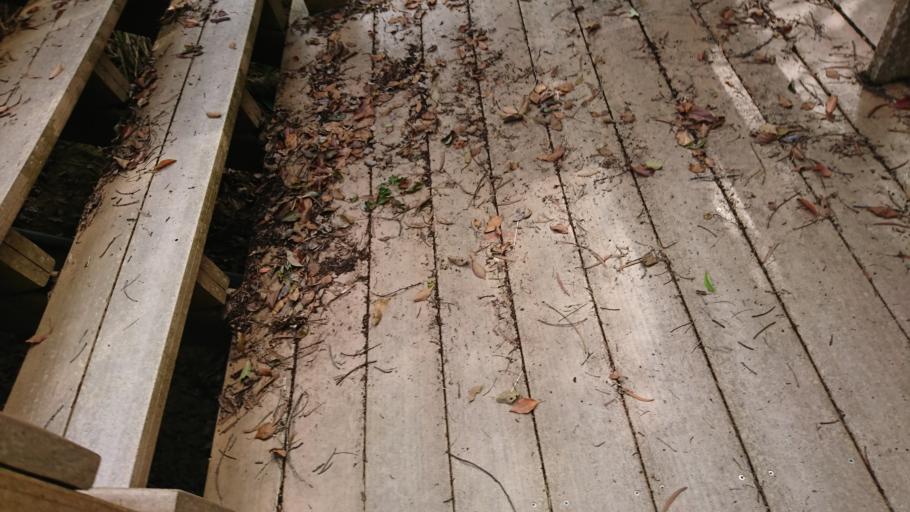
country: TW
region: Taiwan
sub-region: Miaoli
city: Miaoli
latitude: 24.5734
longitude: 120.8517
